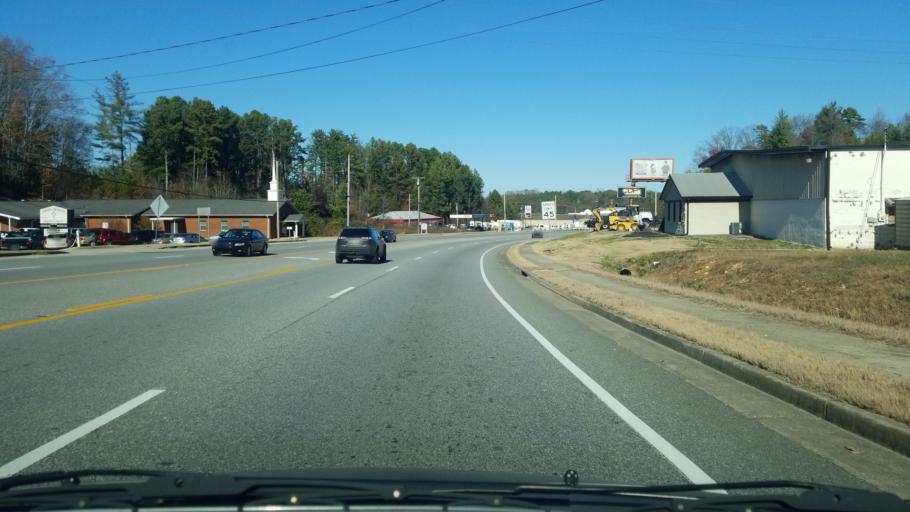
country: US
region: Georgia
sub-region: Catoosa County
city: Indian Springs
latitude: 34.9779
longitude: -85.1889
